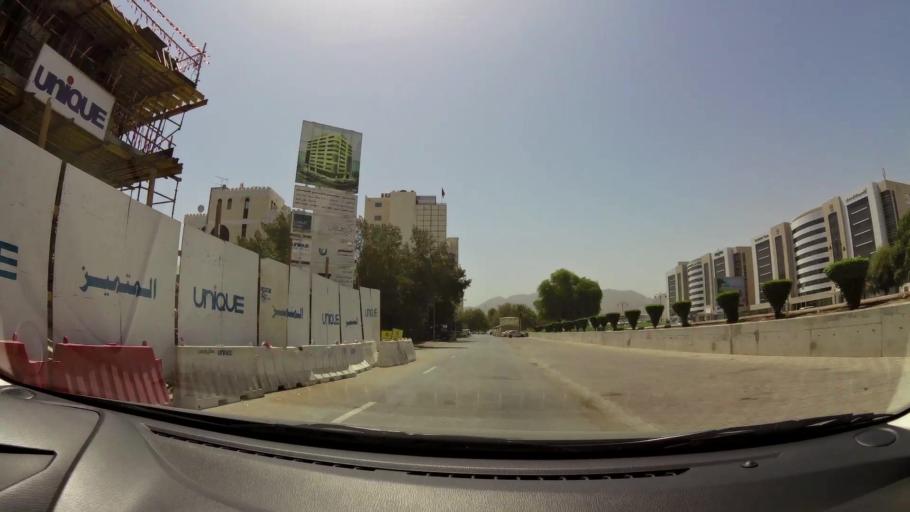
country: OM
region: Muhafazat Masqat
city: Bawshar
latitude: 23.5839
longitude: 58.3972
